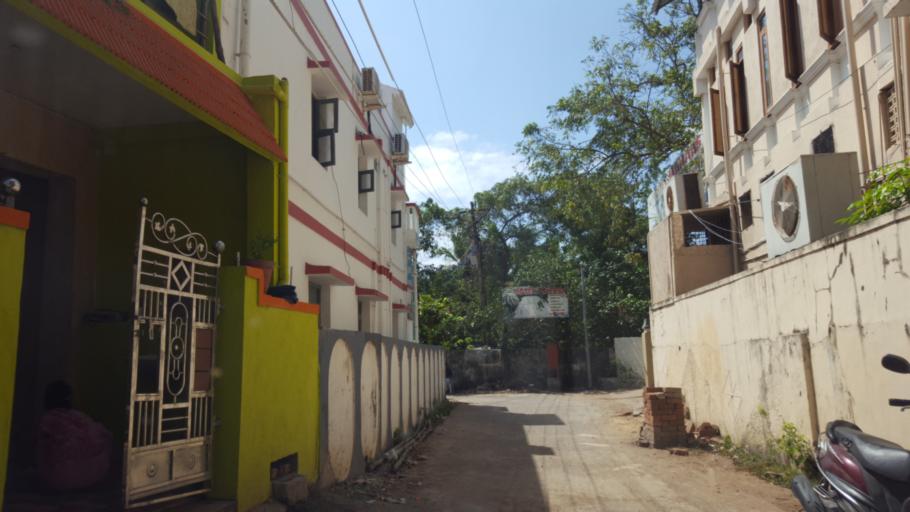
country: IN
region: Tamil Nadu
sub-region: Kancheepuram
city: Mamallapuram
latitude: 12.6176
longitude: 80.1949
